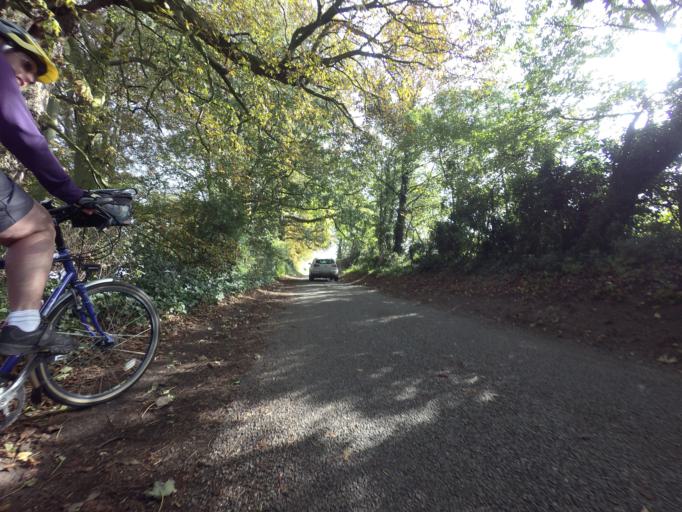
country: GB
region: England
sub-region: Norfolk
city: Snettisham
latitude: 52.8637
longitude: 0.5103
